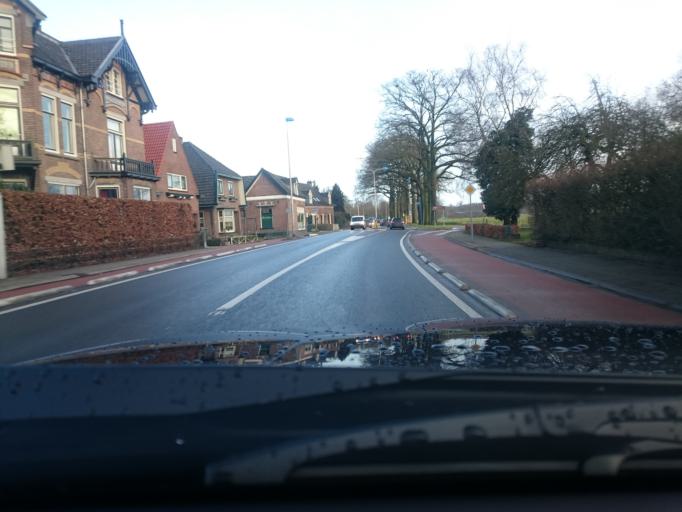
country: NL
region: Gelderland
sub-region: Gemeente Voorst
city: Voorst
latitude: 52.1727
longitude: 6.1416
